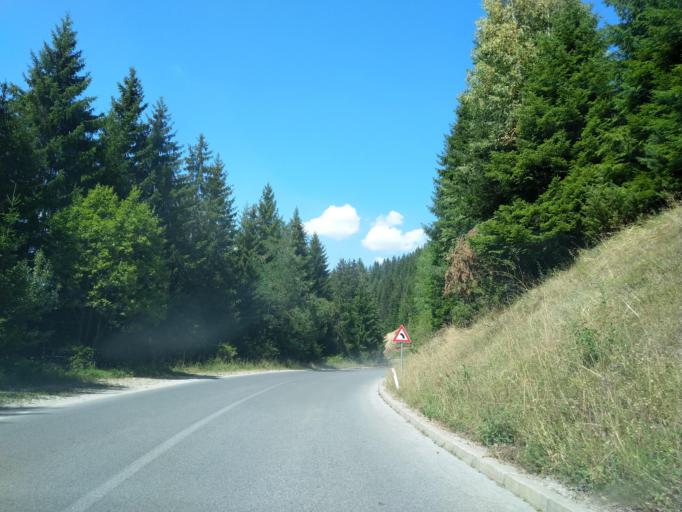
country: RS
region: Central Serbia
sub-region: Zlatiborski Okrug
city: Nova Varos
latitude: 43.4358
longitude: 19.8238
